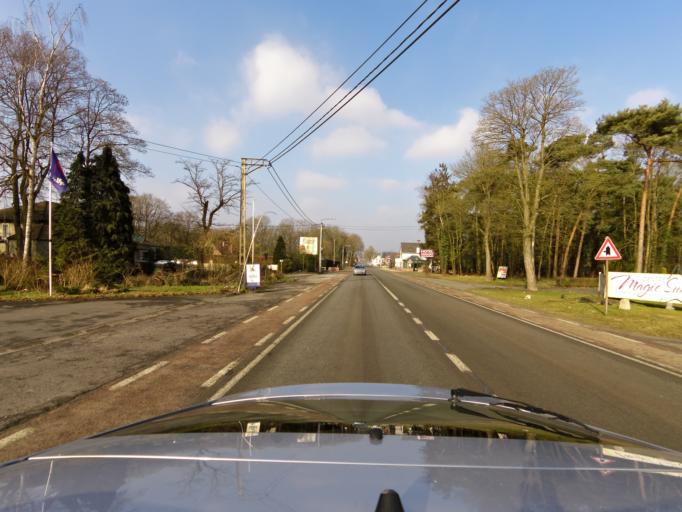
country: BE
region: Wallonia
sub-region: Province du Hainaut
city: Beloeil
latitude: 50.4942
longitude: 3.7184
